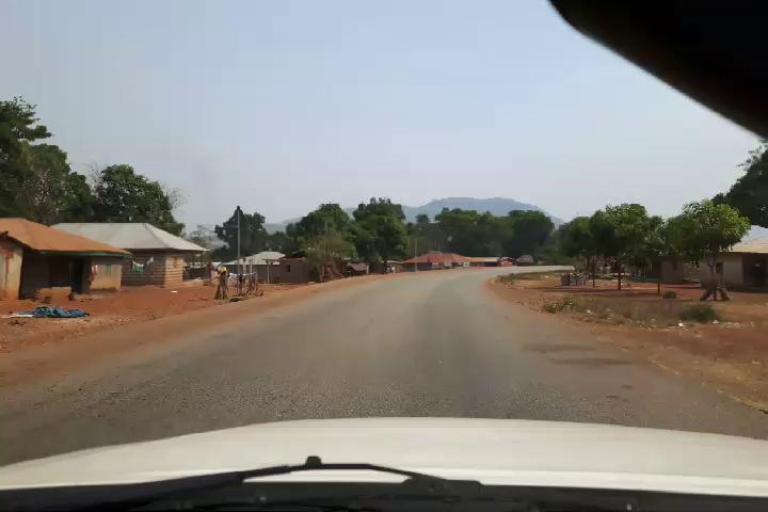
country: SL
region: Northern Province
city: Yonibana
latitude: 8.3997
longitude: -12.1951
